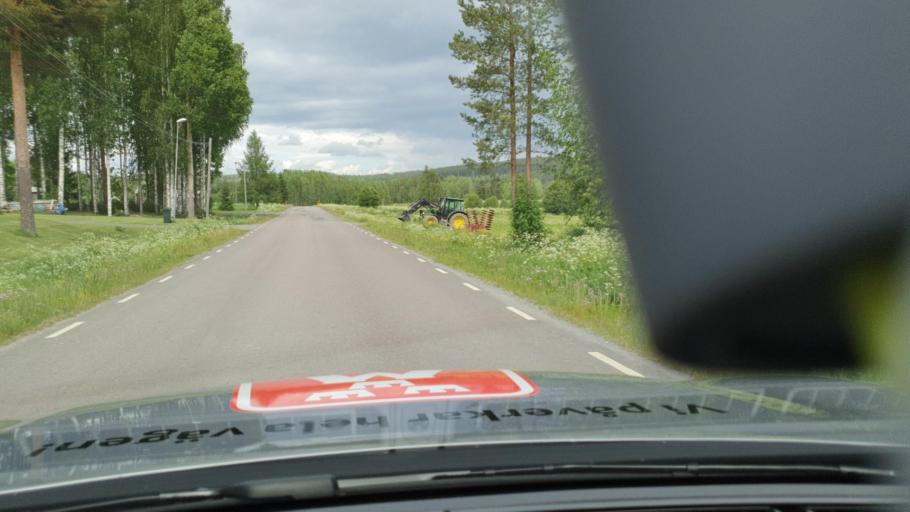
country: SE
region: Norrbotten
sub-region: Lulea Kommun
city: Sodra Sunderbyn
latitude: 65.8503
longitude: 21.9215
